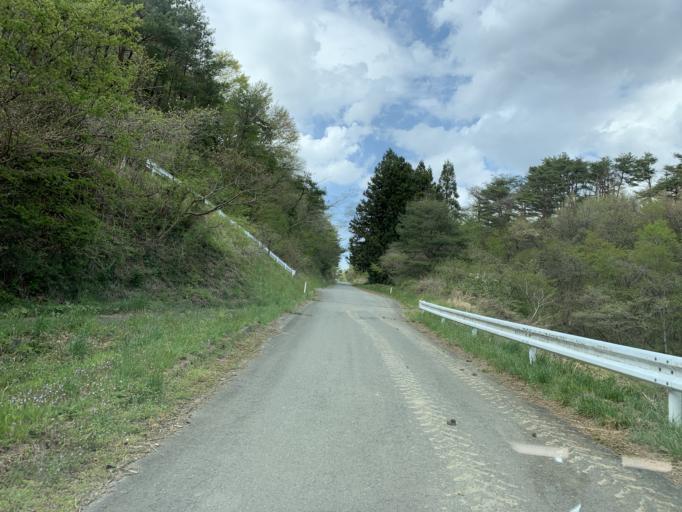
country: JP
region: Iwate
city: Ichinoseki
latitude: 38.7860
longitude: 141.4343
